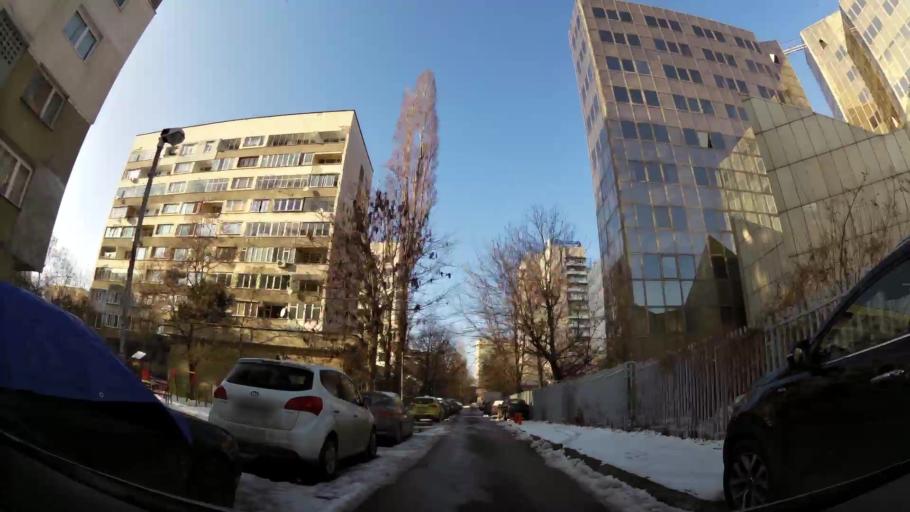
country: BG
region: Sofia-Capital
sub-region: Stolichna Obshtina
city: Sofia
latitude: 42.6698
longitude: 23.3508
